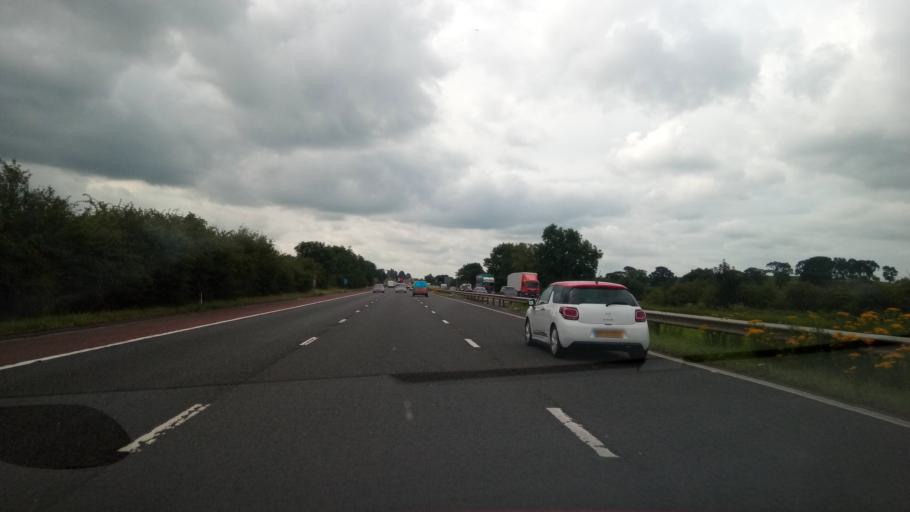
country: GB
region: England
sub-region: Lancashire
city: Galgate
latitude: 53.9928
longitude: -2.7808
